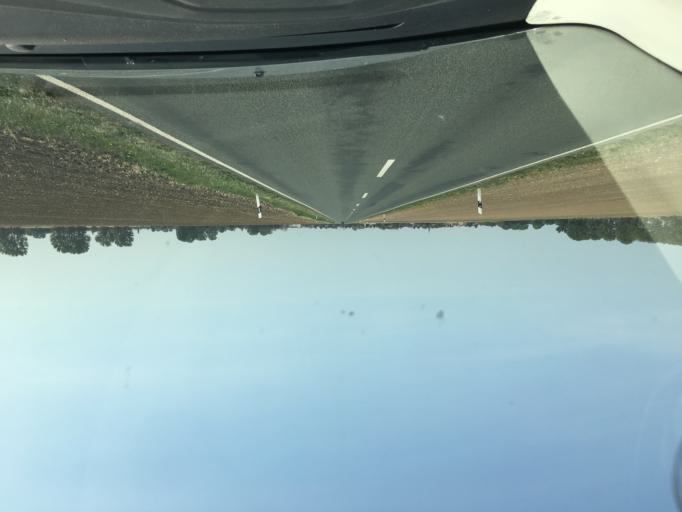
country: DE
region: Saxony-Anhalt
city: Plotzky
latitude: 52.0018
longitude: 11.8155
